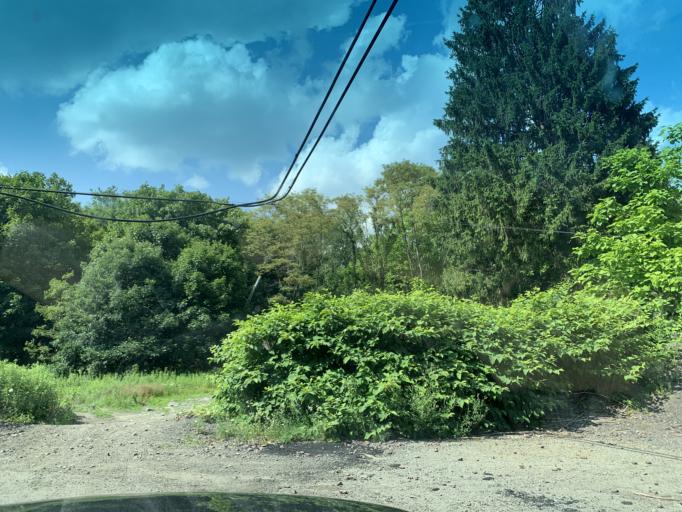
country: US
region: Pennsylvania
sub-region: Schuylkill County
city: Ashland
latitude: 40.8069
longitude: -76.3405
